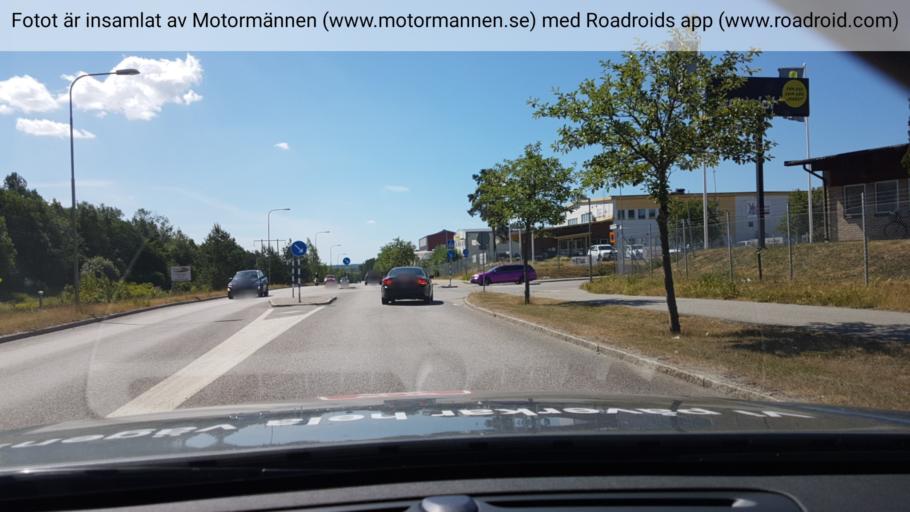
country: SE
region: Stockholm
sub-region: Nacka Kommun
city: Alta
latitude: 59.2403
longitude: 18.1952
